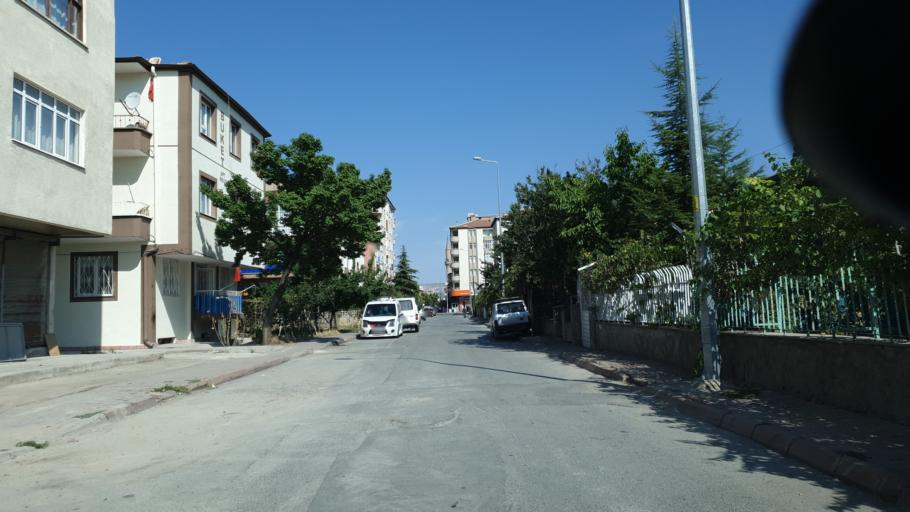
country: TR
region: Kayseri
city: Kayseri
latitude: 38.7374
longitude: 35.4894
